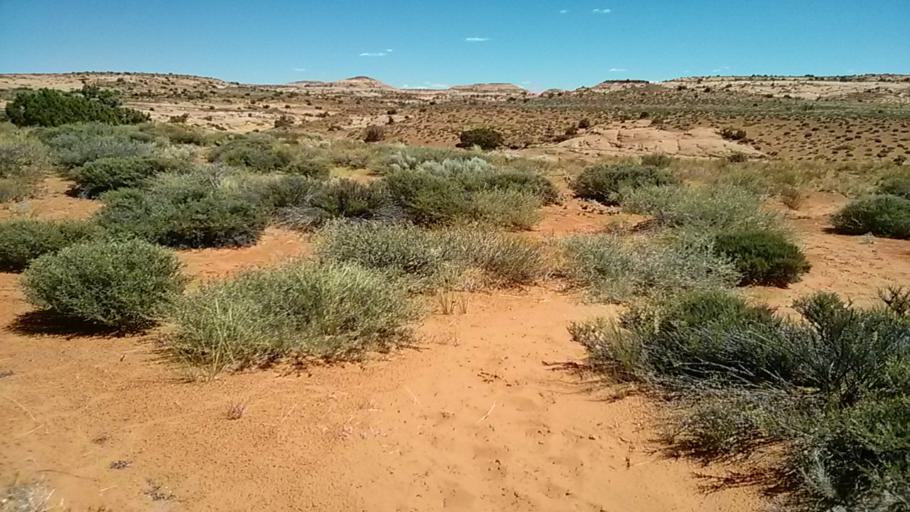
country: US
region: Arizona
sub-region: Coconino County
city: Page
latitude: 37.4850
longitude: -111.2106
